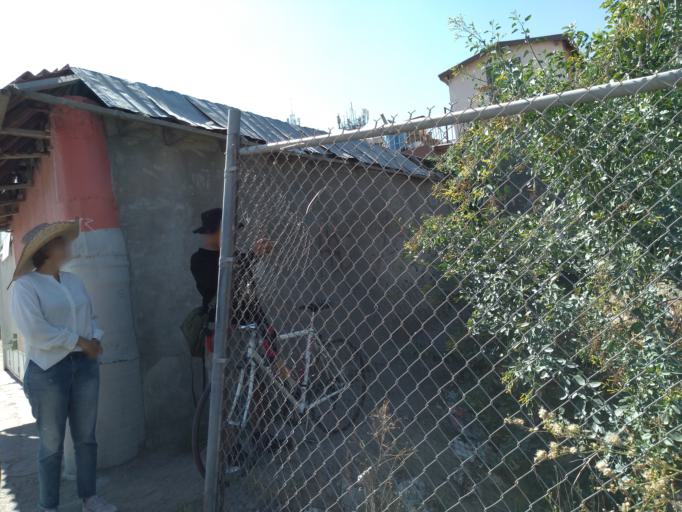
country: US
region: Texas
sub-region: El Paso County
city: El Paso
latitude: 31.7567
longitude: -106.5024
